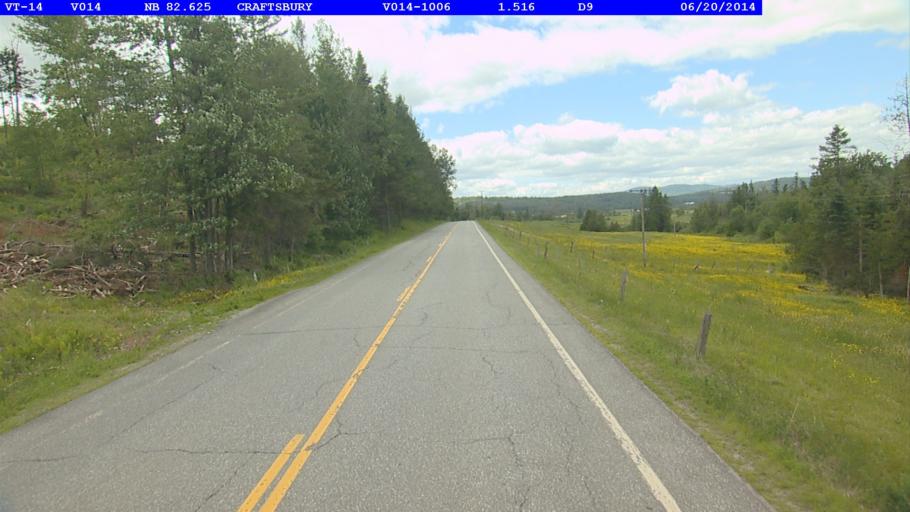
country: US
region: Vermont
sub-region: Caledonia County
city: Hardwick
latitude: 44.6245
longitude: -72.3733
